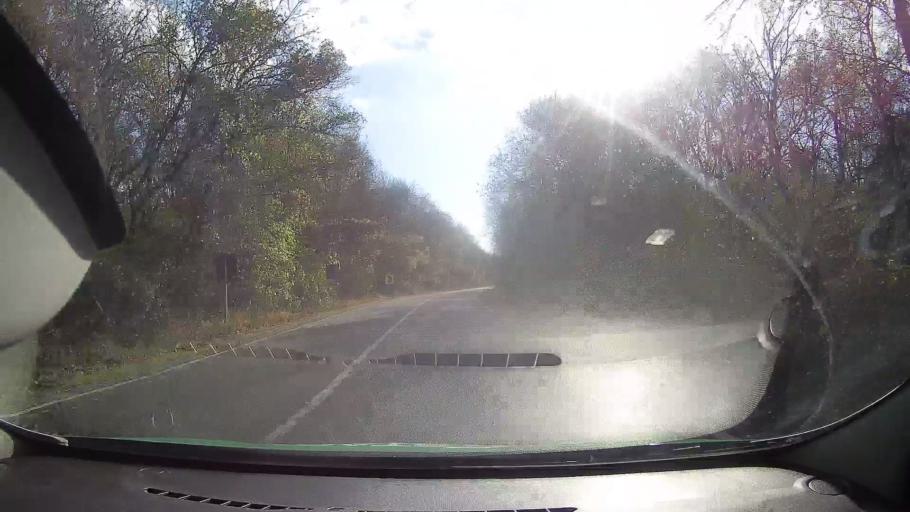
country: RO
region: Tulcea
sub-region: Oras Babadag
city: Babadag
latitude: 44.8498
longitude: 28.6975
